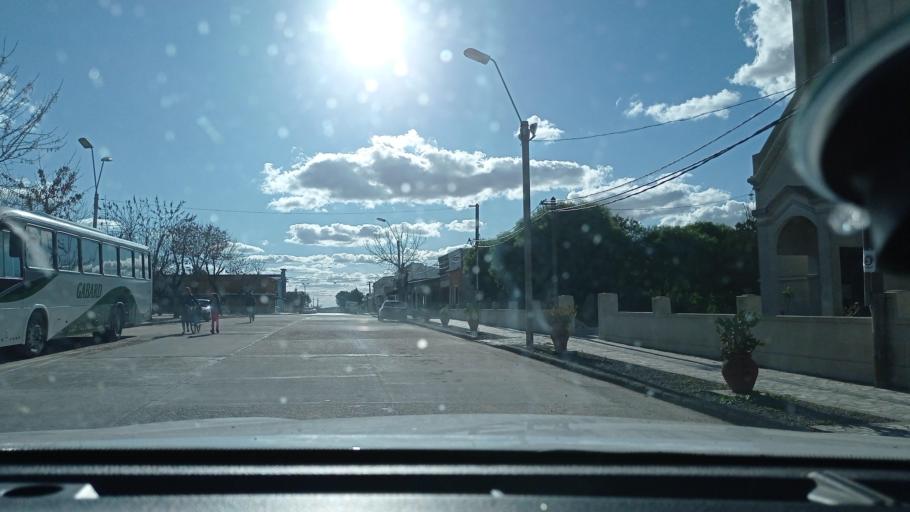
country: UY
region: Florida
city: Casupa
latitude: -34.1005
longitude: -55.6507
